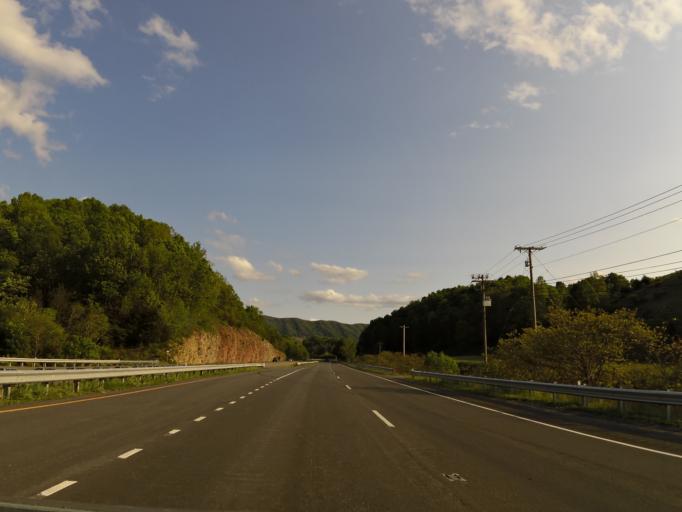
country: US
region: Virginia
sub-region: Tazewell County
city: Claypool Hill
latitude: 37.0253
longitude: -81.7974
